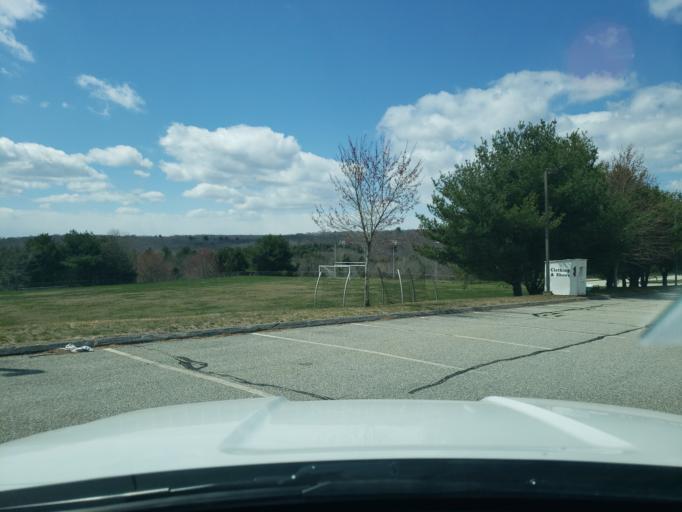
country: US
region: Connecticut
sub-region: New London County
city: Jewett City
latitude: 41.5938
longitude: -71.9805
